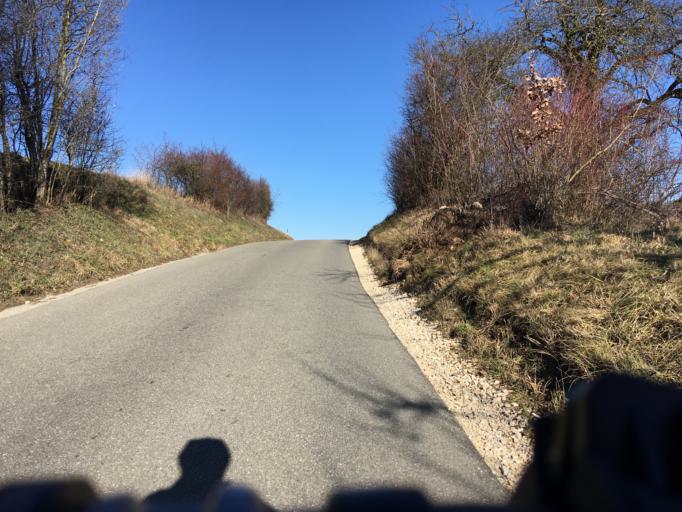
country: CH
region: Schaffhausen
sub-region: Bezirk Reiat
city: Thayngen
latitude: 47.7451
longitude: 8.7424
